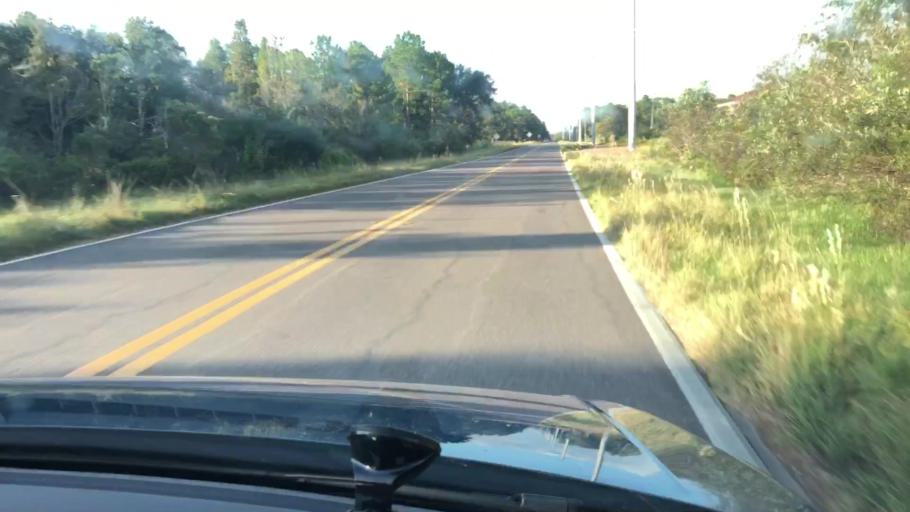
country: US
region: Florida
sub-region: Polk County
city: Polk City
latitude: 28.1454
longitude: -81.8974
